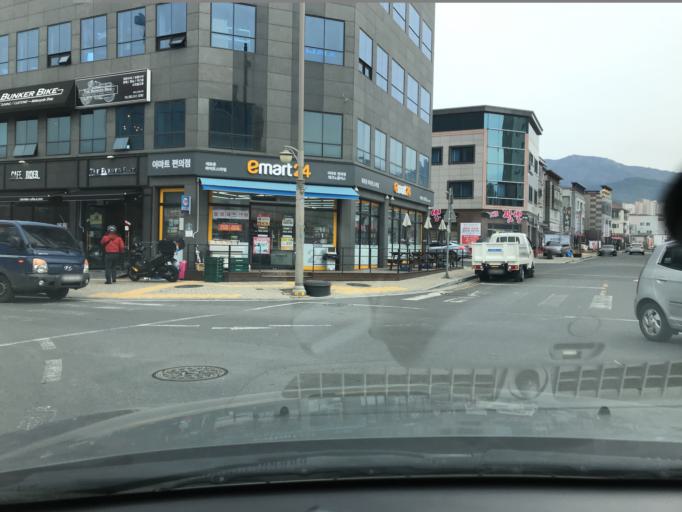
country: KR
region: Daegu
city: Hwawon
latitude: 35.6974
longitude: 128.4545
